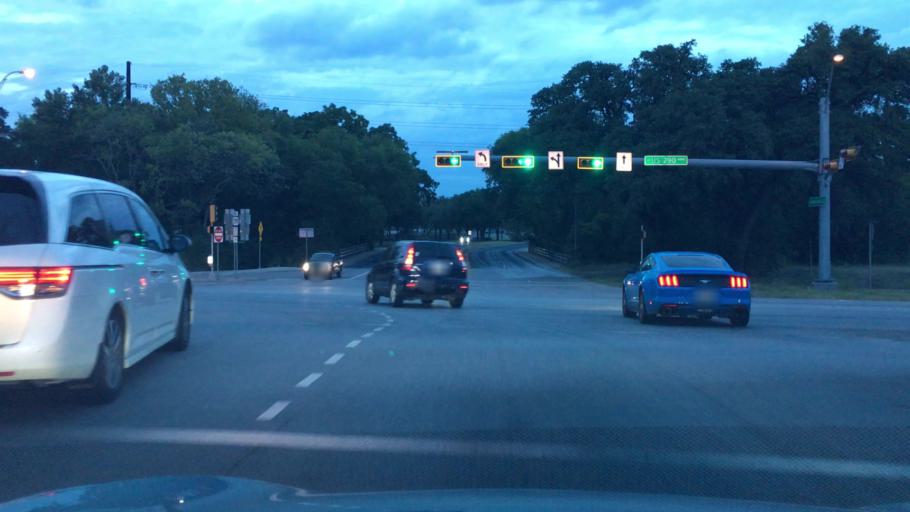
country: US
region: Texas
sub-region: Travis County
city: Barton Creek
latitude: 30.2337
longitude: -97.8647
